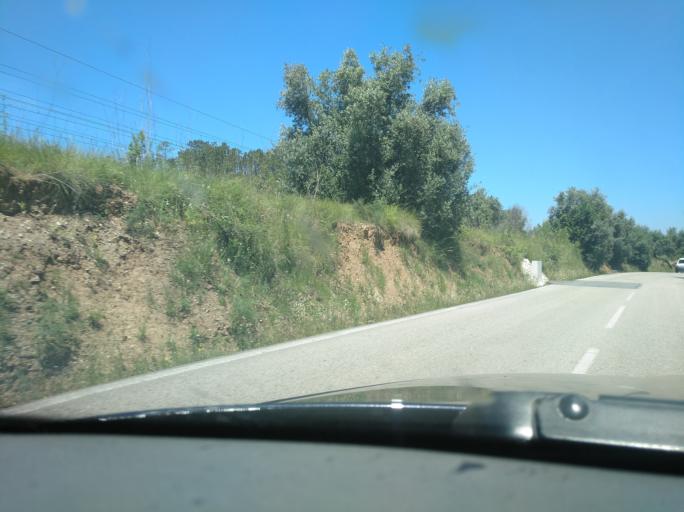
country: PT
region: Aveiro
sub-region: Mealhada
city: Pampilhosa do Botao
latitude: 40.2742
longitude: -8.4342
